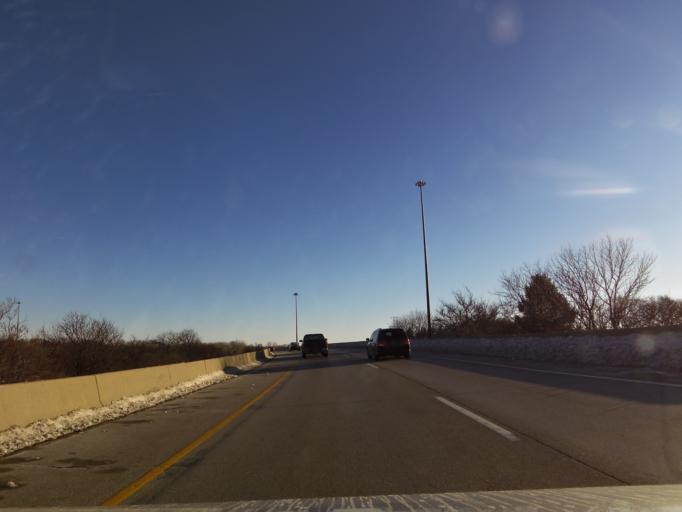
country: US
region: Wisconsin
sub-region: Milwaukee County
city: Greenfield
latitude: 42.9649
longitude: -88.0385
